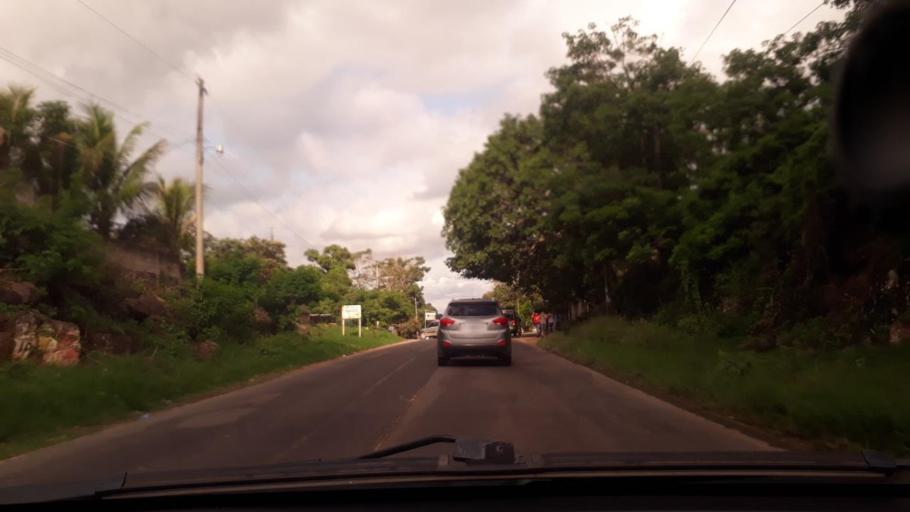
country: GT
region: Jutiapa
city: Quesada
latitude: 14.2774
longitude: -89.9845
